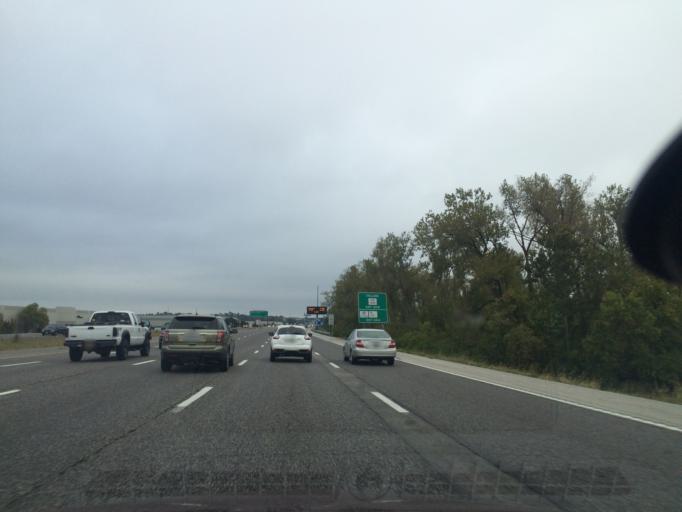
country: US
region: Missouri
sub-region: Saint Charles County
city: Saint Charles
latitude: 38.7619
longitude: -90.4766
